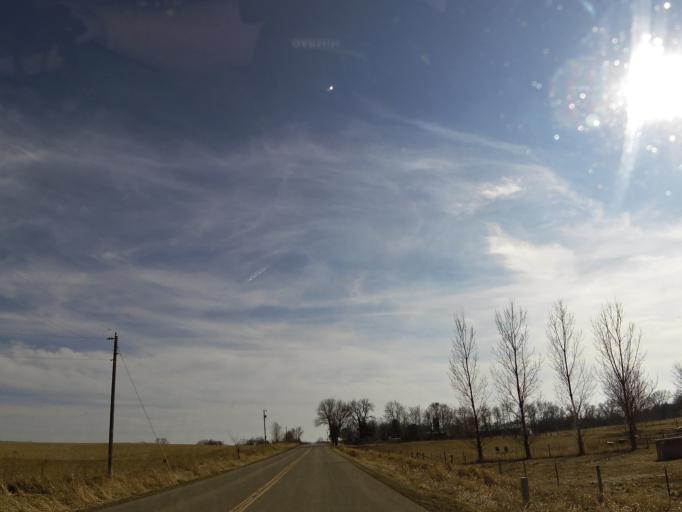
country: US
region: Minnesota
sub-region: Scott County
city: Prior Lake
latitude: 44.6740
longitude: -93.4808
